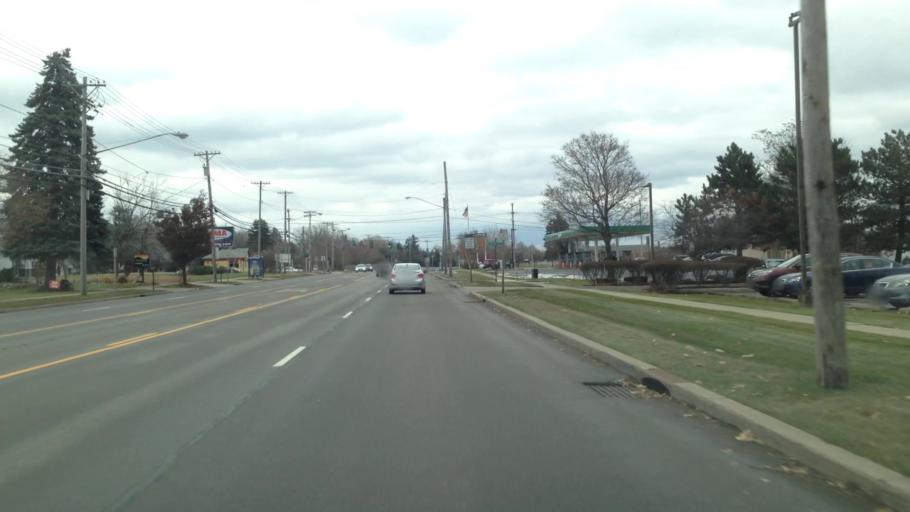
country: US
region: New York
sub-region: Erie County
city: Williamsville
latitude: 42.9656
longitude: -78.7271
